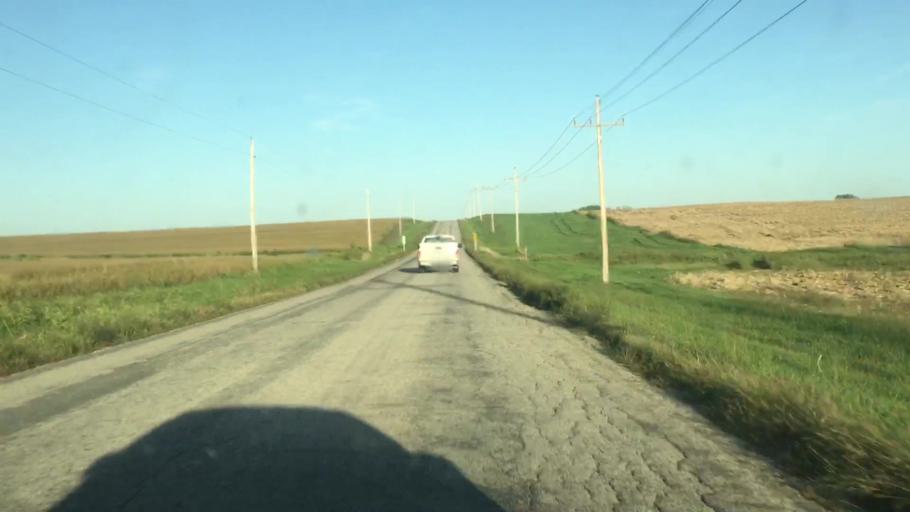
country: US
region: Kansas
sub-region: Brown County
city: Horton
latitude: 39.5656
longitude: -95.3727
